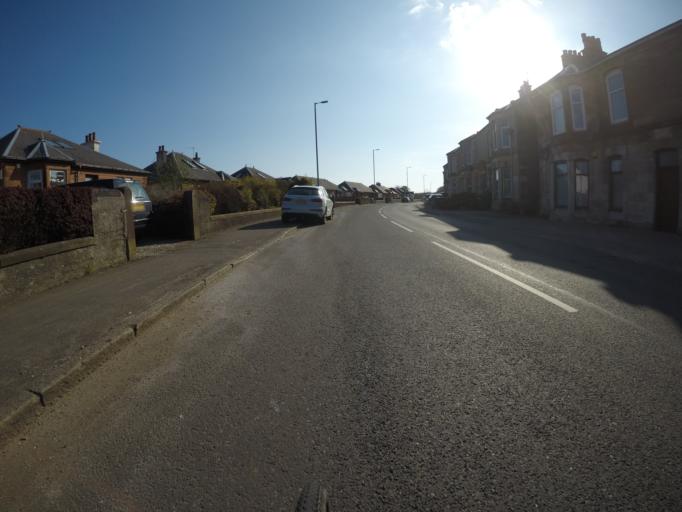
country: GB
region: Scotland
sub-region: North Ayrshire
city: Kilwinning
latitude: 55.6527
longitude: -4.7156
